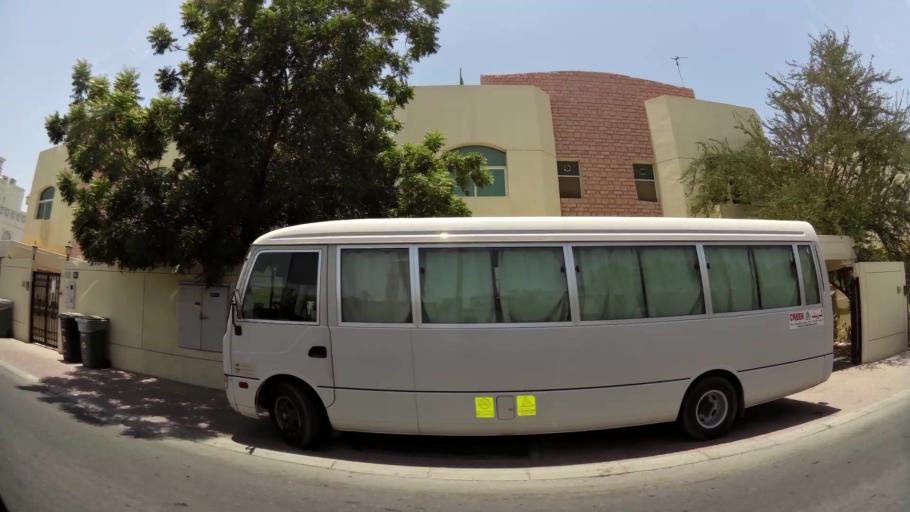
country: AE
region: Ash Shariqah
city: Sharjah
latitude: 25.2326
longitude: 55.2693
